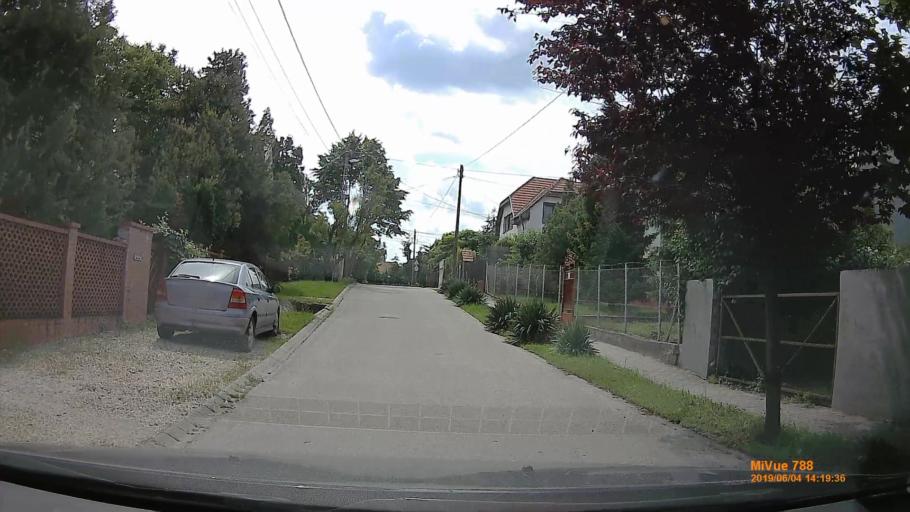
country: HU
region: Budapest
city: Budapest XXII. keruelet
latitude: 47.4175
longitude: 19.0020
